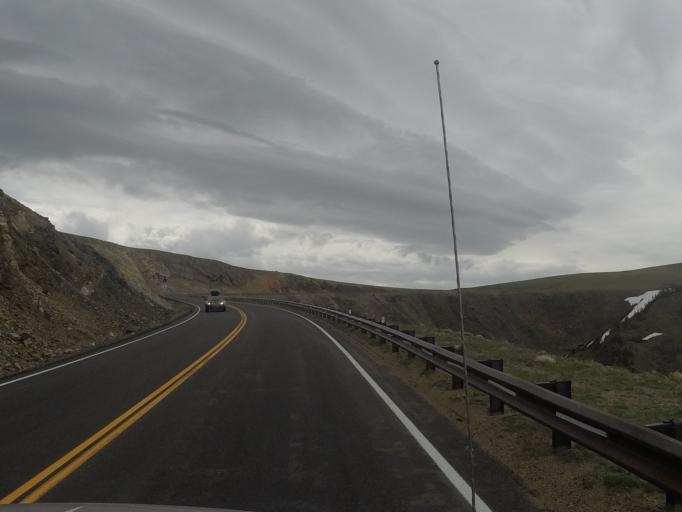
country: US
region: Montana
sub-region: Carbon County
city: Red Lodge
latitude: 45.0306
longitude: -109.4113
